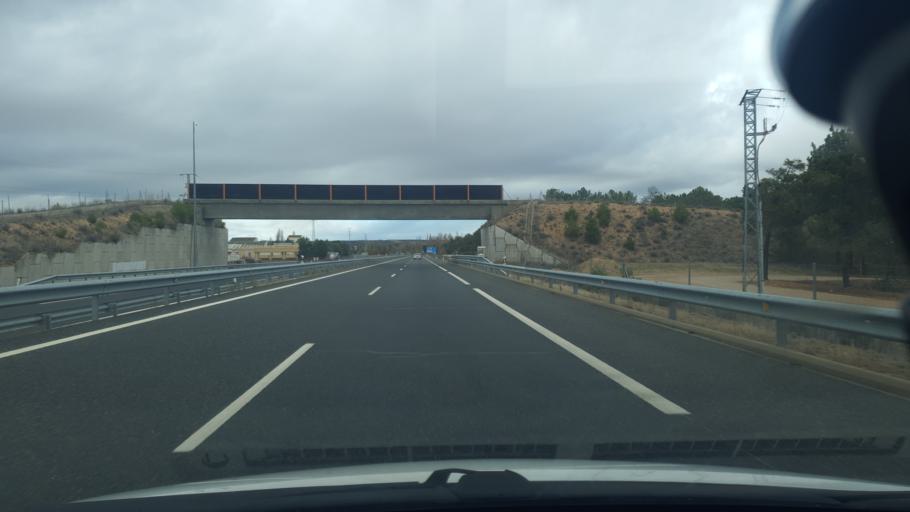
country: ES
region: Castille and Leon
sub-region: Provincia de Segovia
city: Sanchonuno
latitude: 41.3572
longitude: -4.2994
